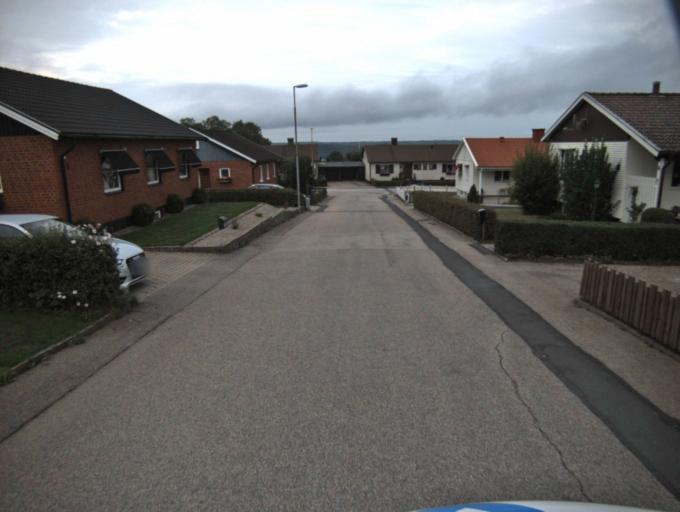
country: SE
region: Vaestra Goetaland
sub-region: Ulricehamns Kommun
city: Ulricehamn
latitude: 57.7993
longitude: 13.4290
